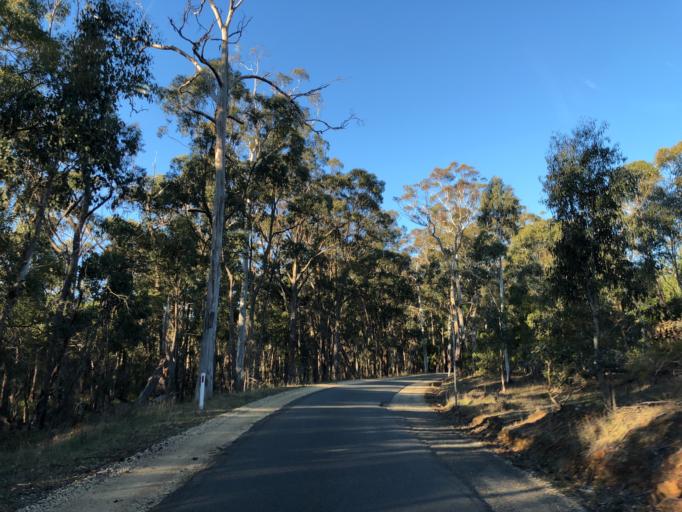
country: AU
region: Victoria
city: Brown Hill
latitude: -37.4884
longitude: 144.1370
